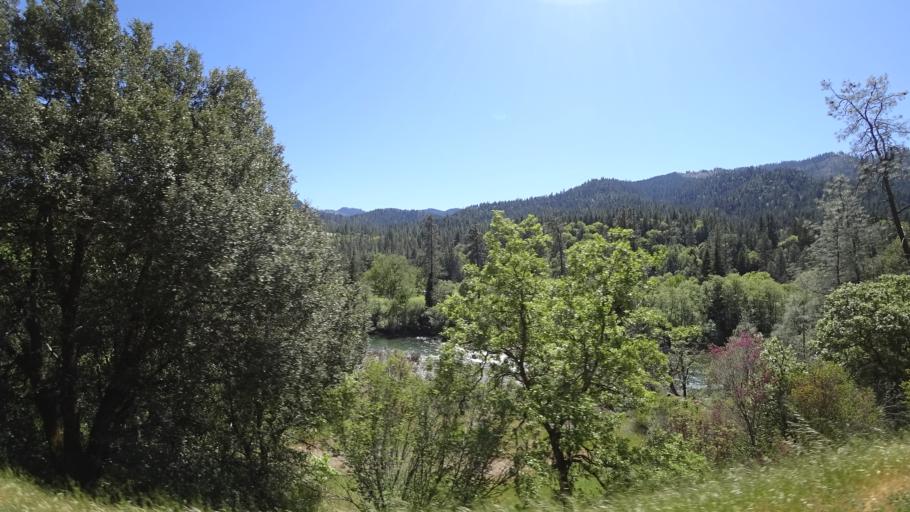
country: US
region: California
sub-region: Trinity County
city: Hayfork
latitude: 40.7417
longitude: -123.2635
